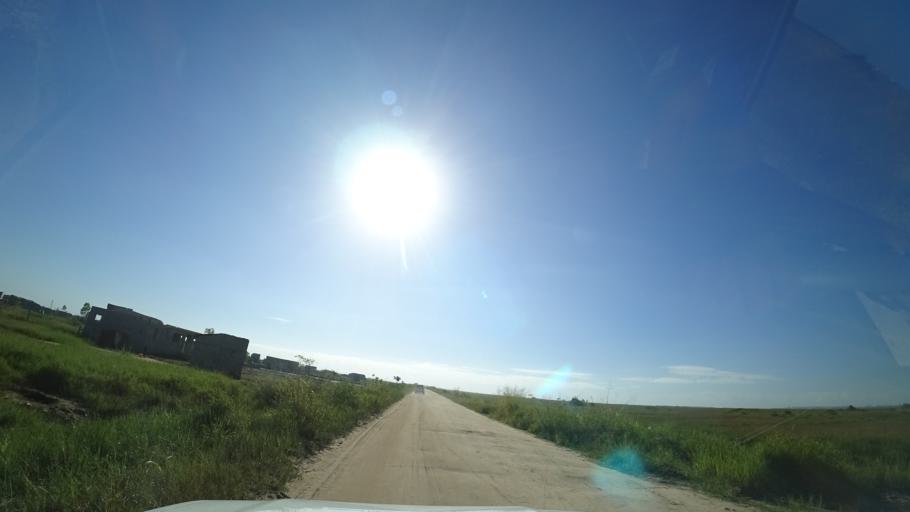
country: MZ
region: Sofala
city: Beira
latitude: -19.7619
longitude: 34.9091
